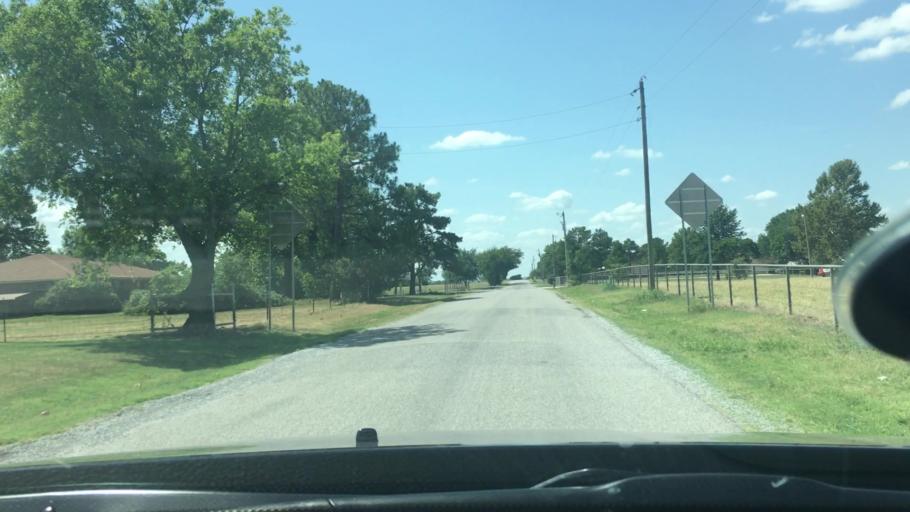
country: US
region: Oklahoma
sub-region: Love County
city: Marietta
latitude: 33.9388
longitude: -97.1608
